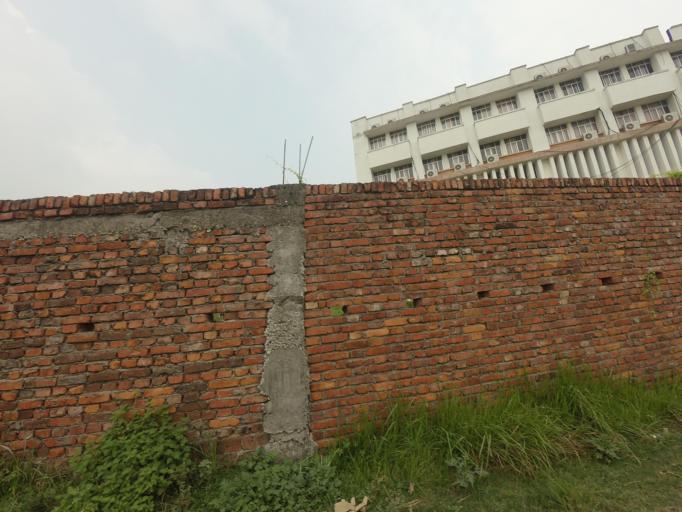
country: NP
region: Western Region
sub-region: Lumbini Zone
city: Bhairahawa
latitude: 27.4873
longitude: 83.4487
